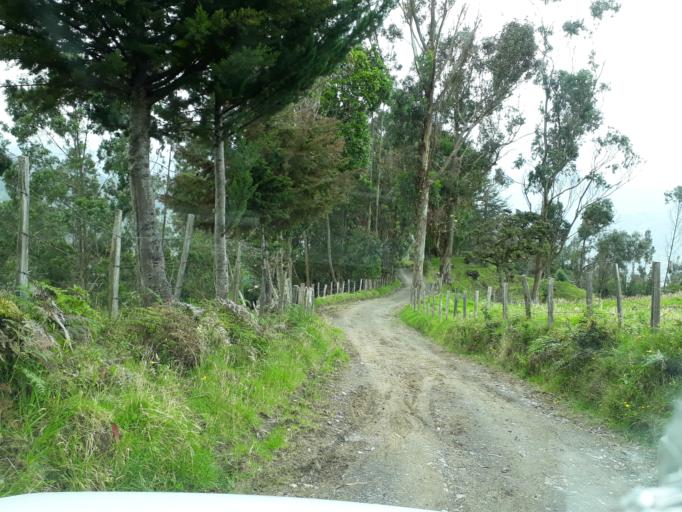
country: CO
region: Cundinamarca
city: Junin
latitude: 4.7519
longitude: -73.6281
